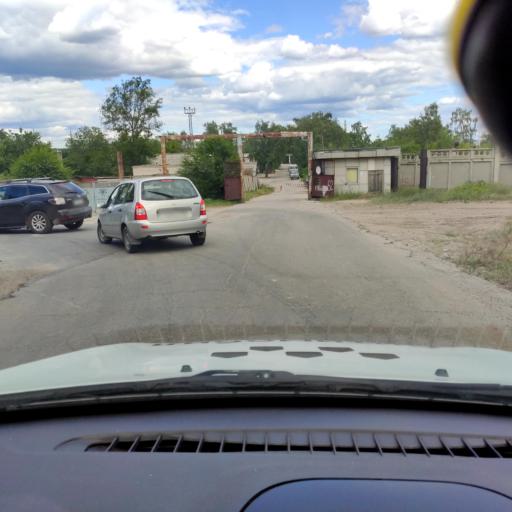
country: RU
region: Samara
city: Zhigulevsk
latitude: 53.4677
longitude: 49.5134
